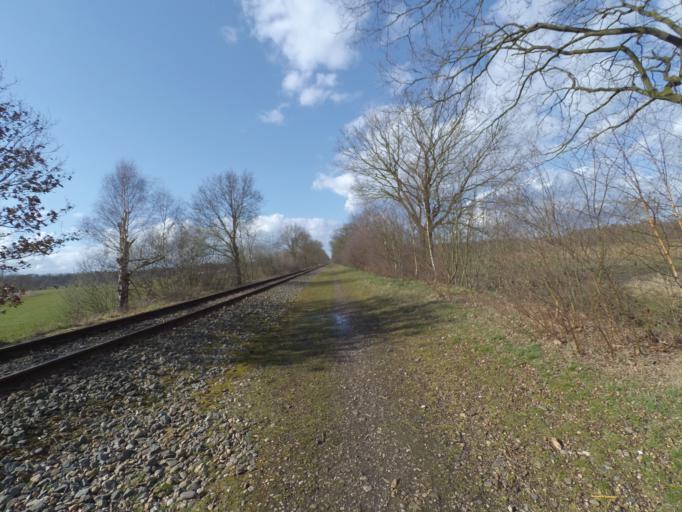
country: NL
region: Utrecht
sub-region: Gemeente Amersfoort
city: Randenbroek
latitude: 52.1261
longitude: 5.4089
